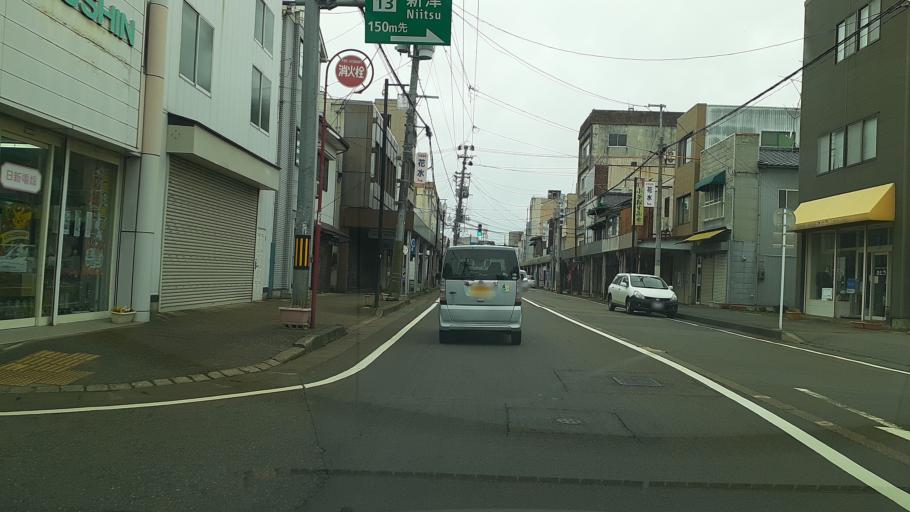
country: JP
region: Niigata
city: Niitsu-honcho
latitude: 37.7949
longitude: 139.1258
